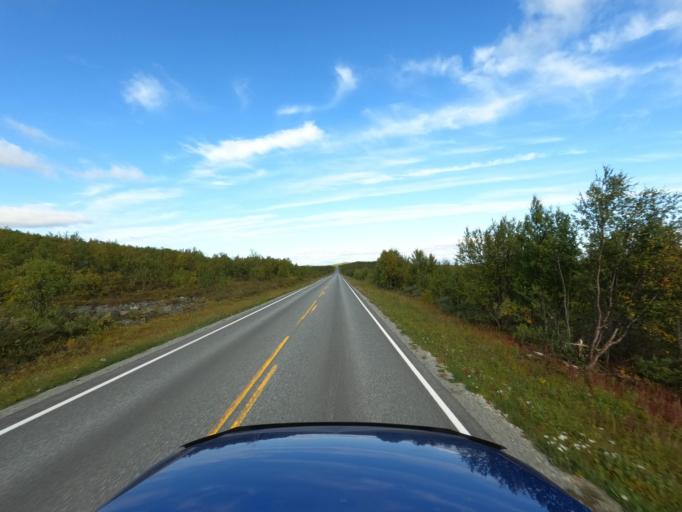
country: NO
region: Finnmark Fylke
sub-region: Karasjok
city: Karasjohka
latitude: 69.6876
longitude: 25.2608
